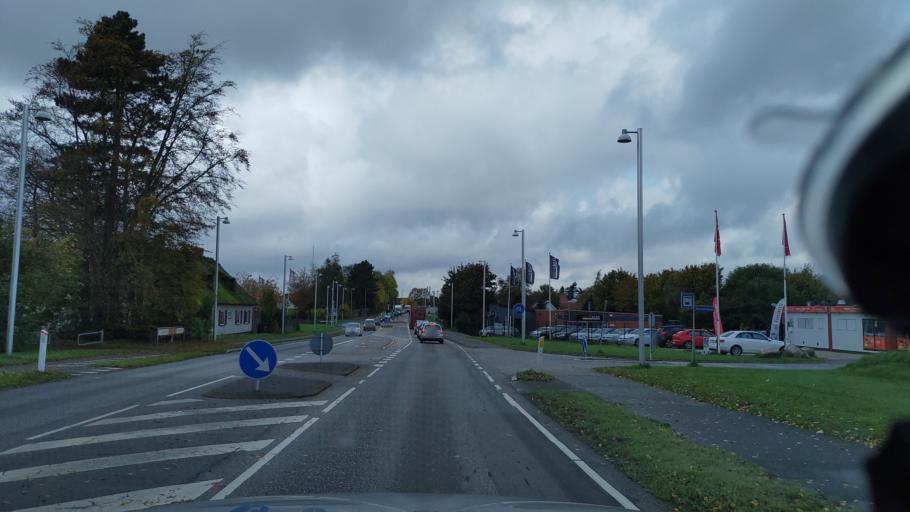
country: DK
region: Zealand
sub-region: Naestved Kommune
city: Fensmark
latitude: 55.2594
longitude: 11.8525
